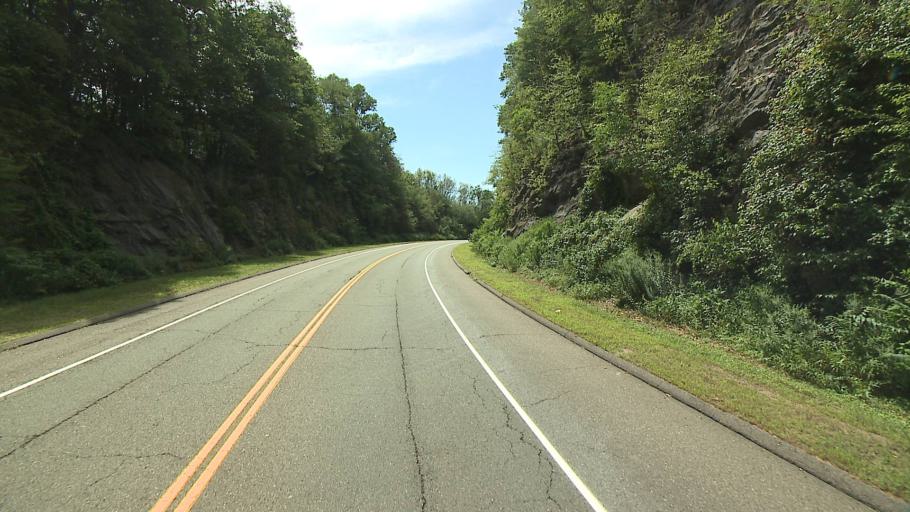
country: US
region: Connecticut
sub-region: Hartford County
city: Collinsville
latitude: 41.8072
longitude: -72.9252
